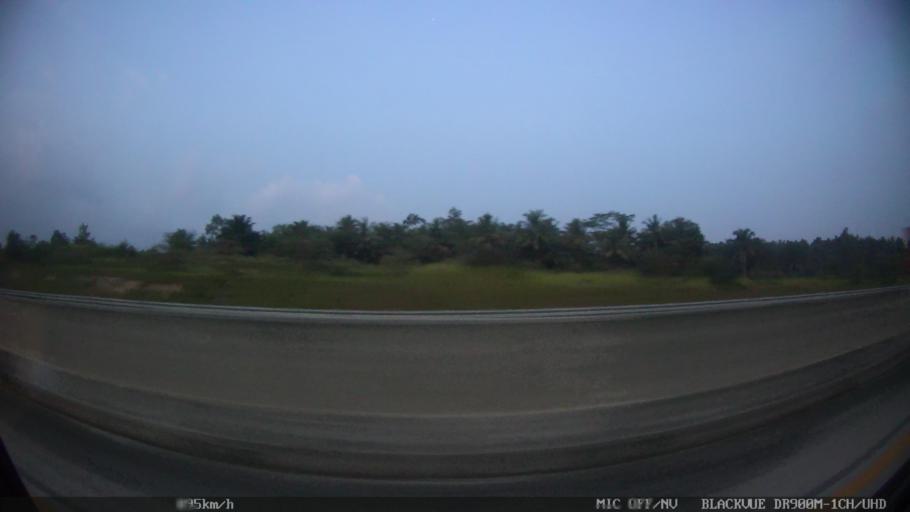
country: ID
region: Lampung
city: Sidorejo
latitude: -5.5516
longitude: 105.5250
